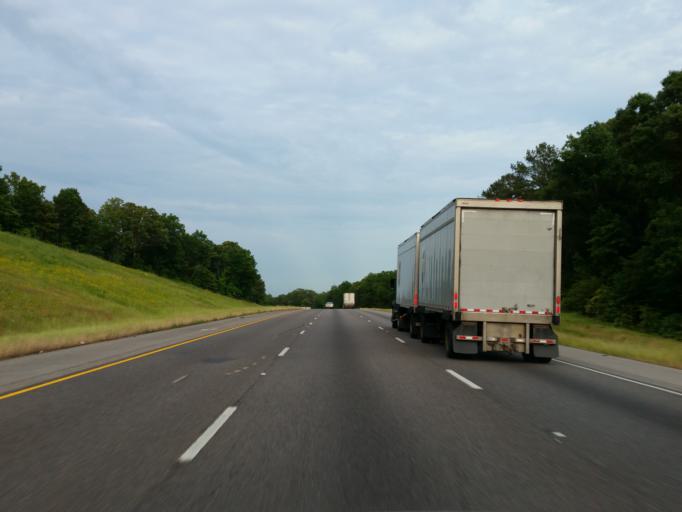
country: US
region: Alabama
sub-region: Calhoun County
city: Bynum
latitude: 33.5758
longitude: -85.9980
